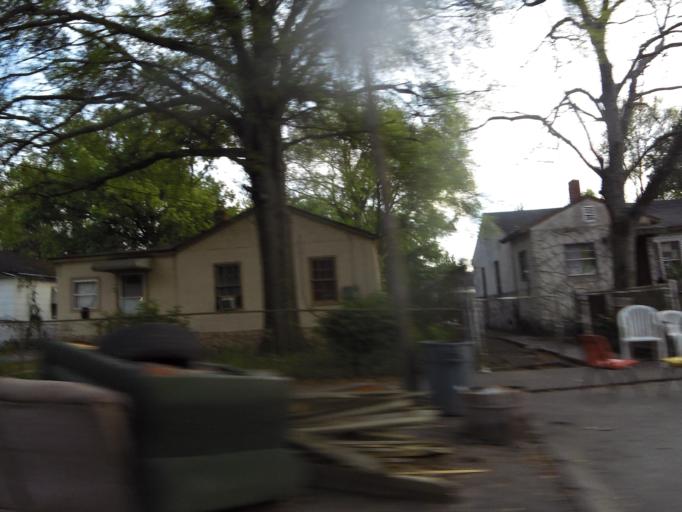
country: US
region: Florida
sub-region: Duval County
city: Jacksonville
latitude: 30.3604
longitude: -81.6297
